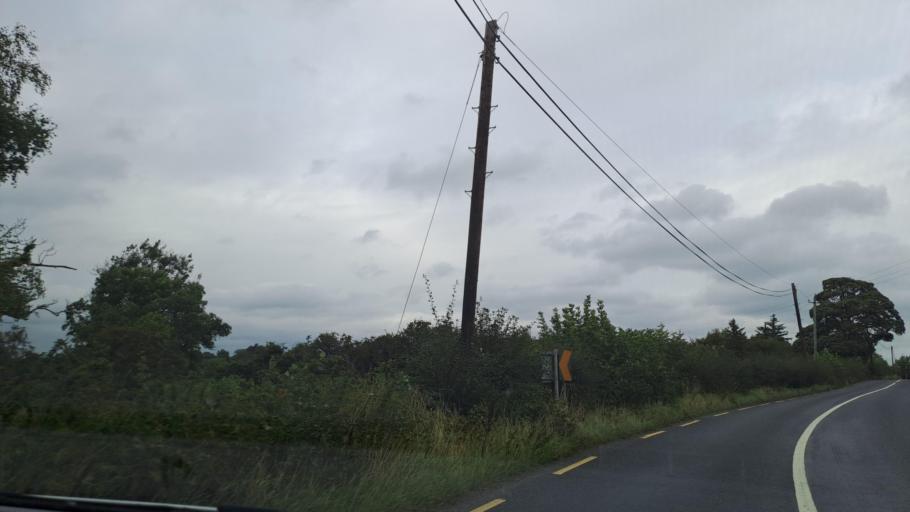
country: IE
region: Ulster
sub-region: An Cabhan
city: Bailieborough
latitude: 53.9374
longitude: -6.9652
